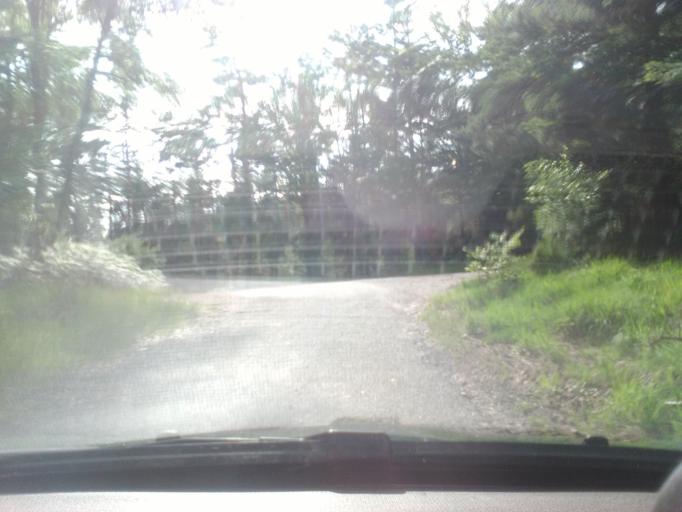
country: FR
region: Lorraine
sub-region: Departement des Vosges
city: Granges-sur-Vologne
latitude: 48.2237
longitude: 6.8045
